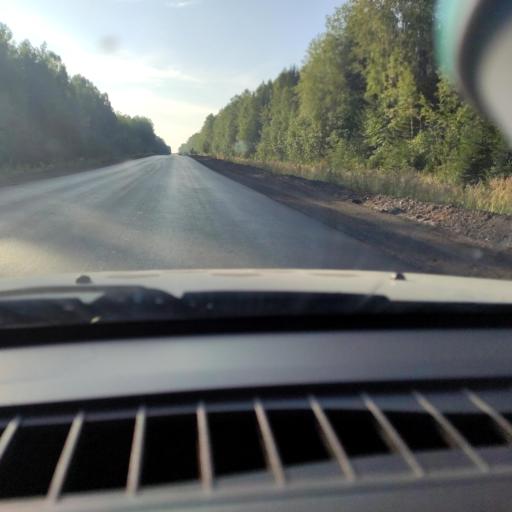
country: RU
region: Kirov
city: Chernaya Kholunitsa
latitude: 58.8801
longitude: 51.4445
